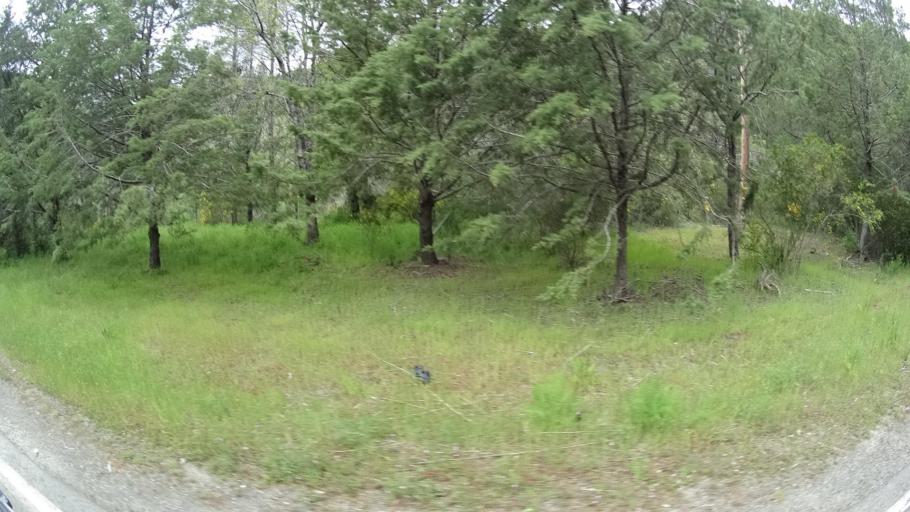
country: US
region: California
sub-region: Humboldt County
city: Redway
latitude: 40.1272
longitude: -123.8671
